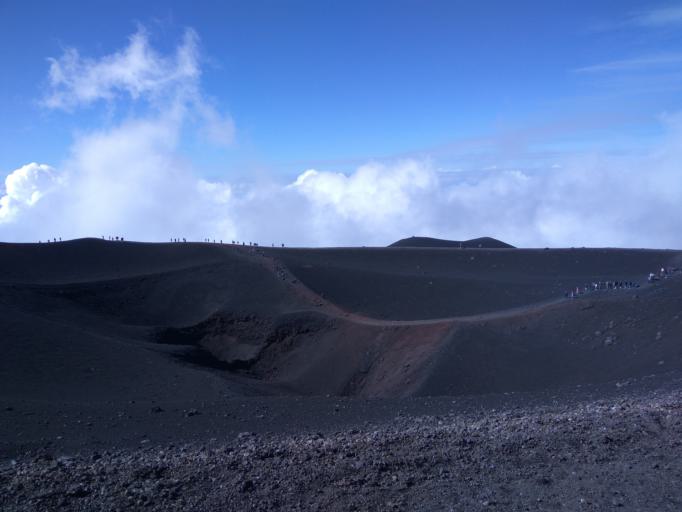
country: IT
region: Sicily
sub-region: Catania
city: Ragalna
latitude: 37.7359
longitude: 15.0011
